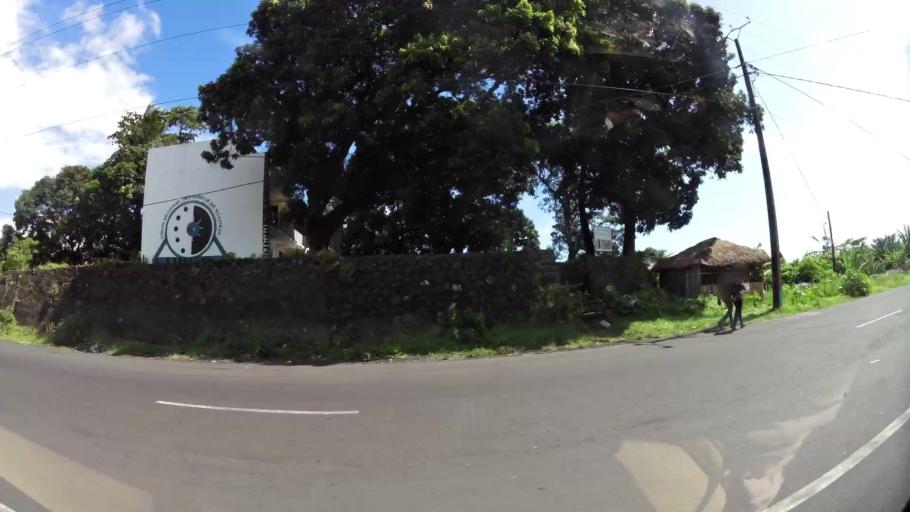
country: KM
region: Grande Comore
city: Mavingouni
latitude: -11.7124
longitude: 43.2460
